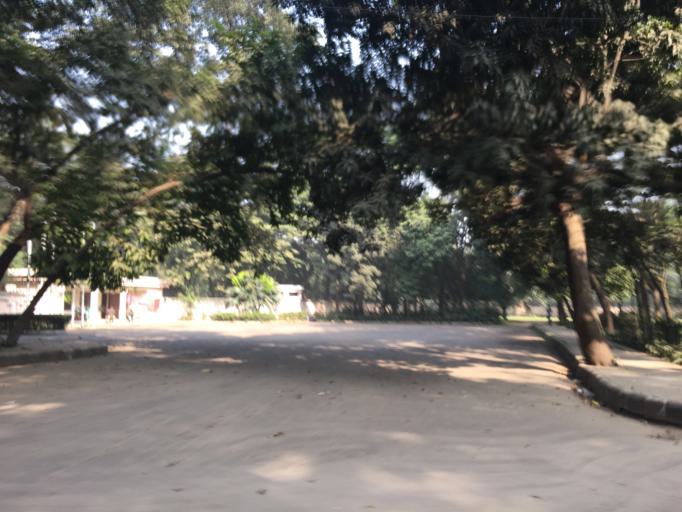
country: BD
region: Dhaka
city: Paltan
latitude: 23.7409
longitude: 90.4000
